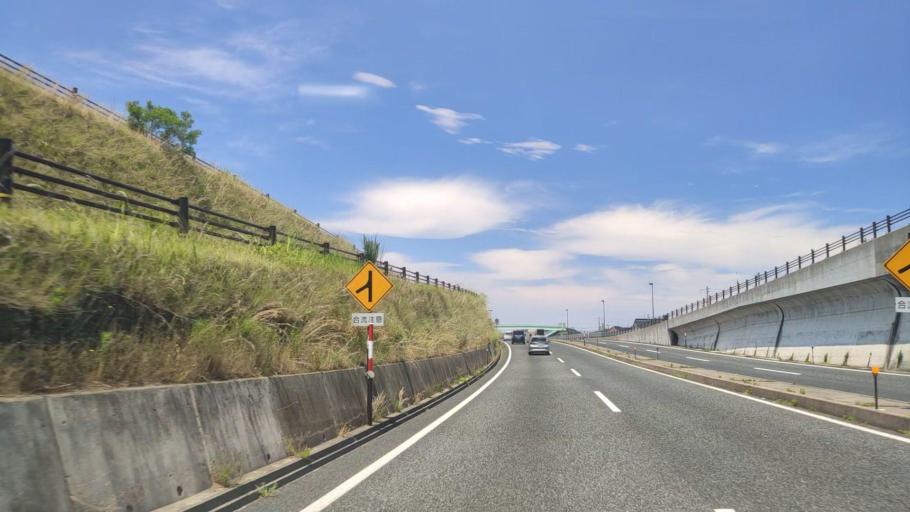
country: JP
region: Tottori
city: Tottori
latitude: 35.4995
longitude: 134.2179
